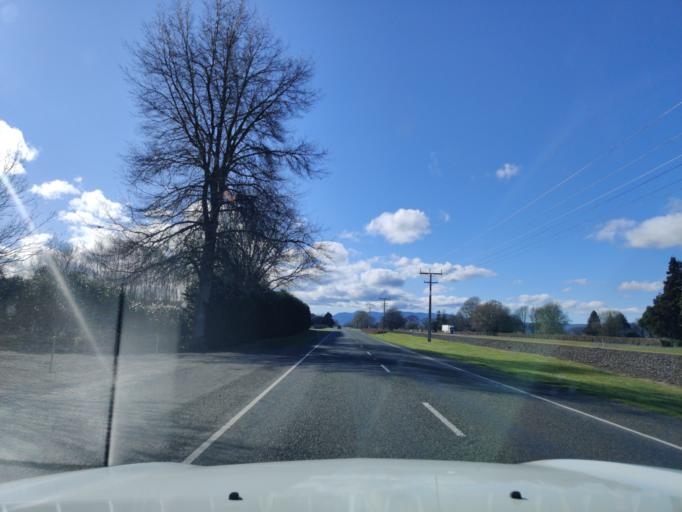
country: NZ
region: Waikato
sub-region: Matamata-Piako District
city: Matamata
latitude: -37.8498
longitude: 175.7596
